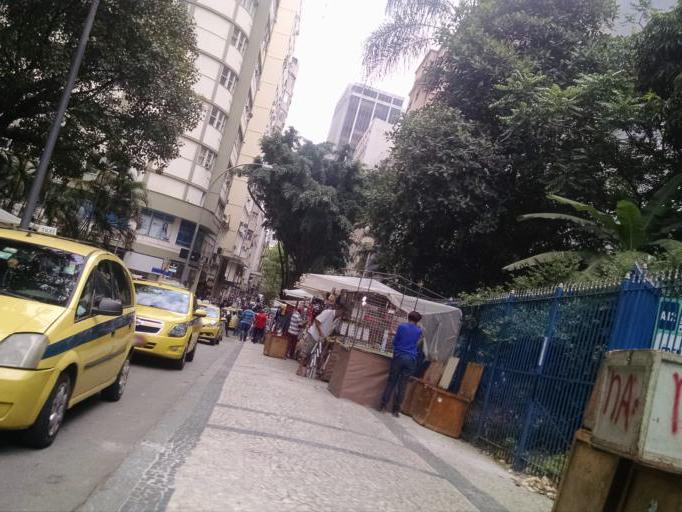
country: BR
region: Rio de Janeiro
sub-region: Rio De Janeiro
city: Rio de Janeiro
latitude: -22.9058
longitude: -43.1757
